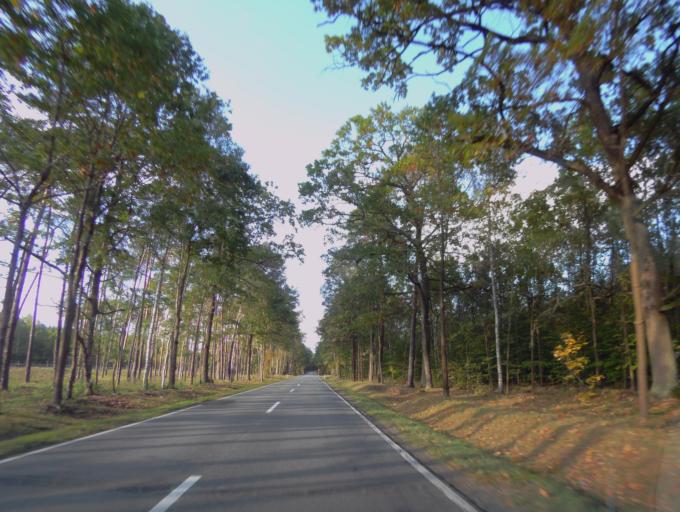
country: PL
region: Subcarpathian Voivodeship
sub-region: Powiat nizanski
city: Krzeszow
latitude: 50.3812
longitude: 22.3097
